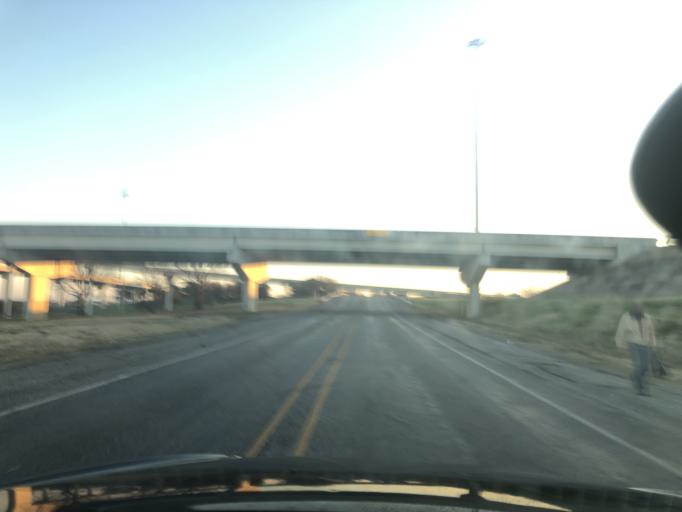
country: US
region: Texas
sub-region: Tarrant County
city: White Settlement
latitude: 32.7392
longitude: -97.4835
